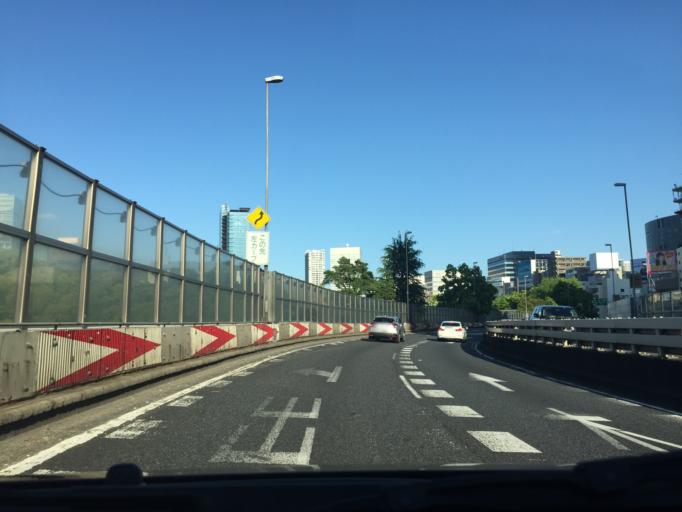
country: JP
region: Tokyo
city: Tokyo
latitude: 35.6548
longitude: 139.7452
